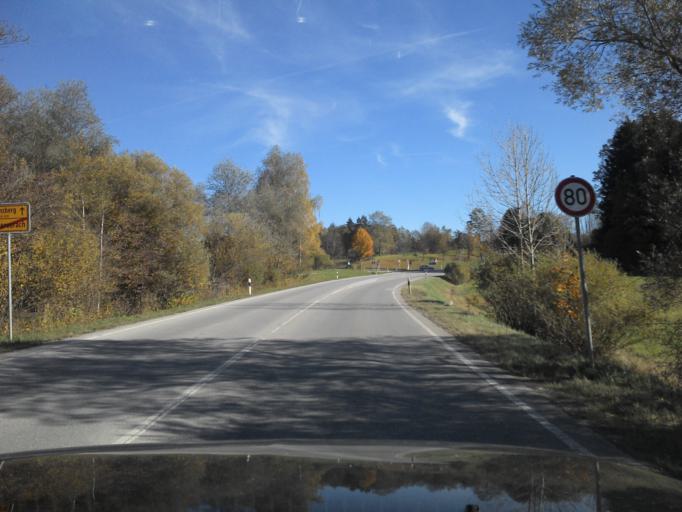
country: DE
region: Bavaria
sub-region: Upper Bavaria
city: Iffeldorf
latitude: 47.7737
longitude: 11.3378
